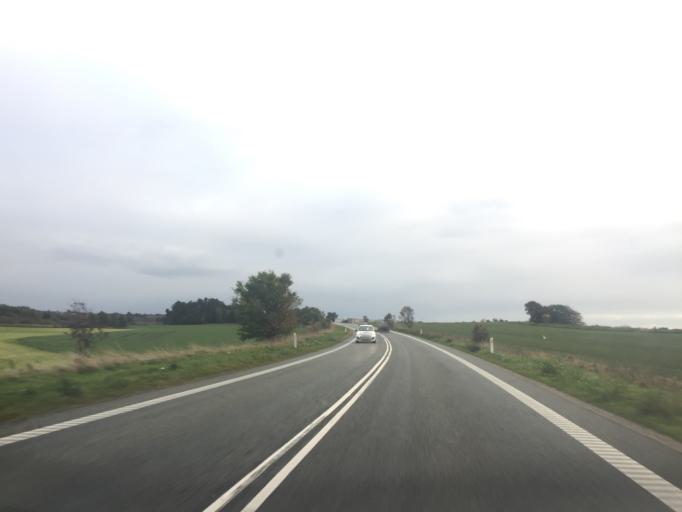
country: DK
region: Capital Region
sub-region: Egedal Kommune
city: Smorumnedre
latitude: 55.7701
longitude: 12.2928
